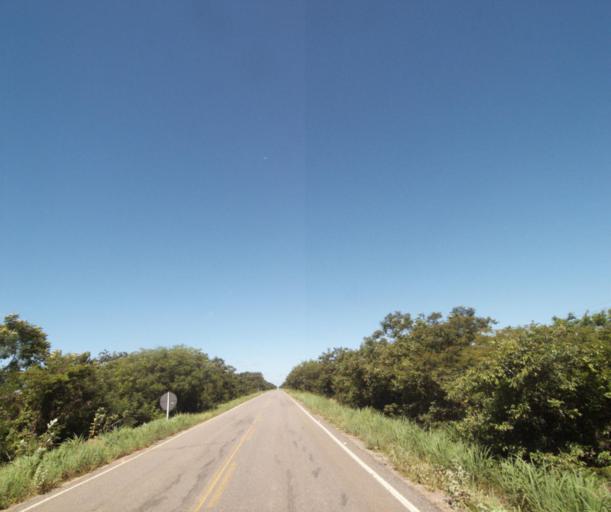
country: BR
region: Bahia
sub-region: Carinhanha
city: Carinhanha
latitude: -14.2825
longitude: -43.5588
